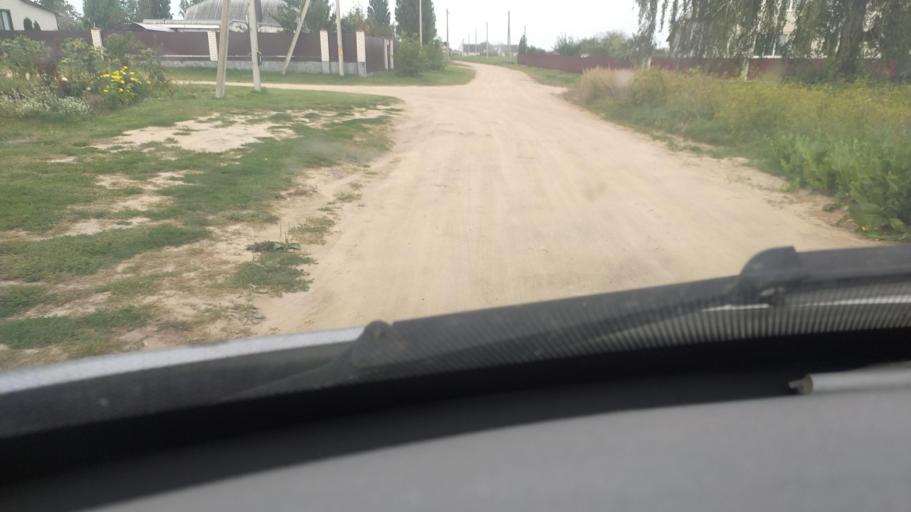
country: BY
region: Brest
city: Byaroza
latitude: 52.5540
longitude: 24.9663
